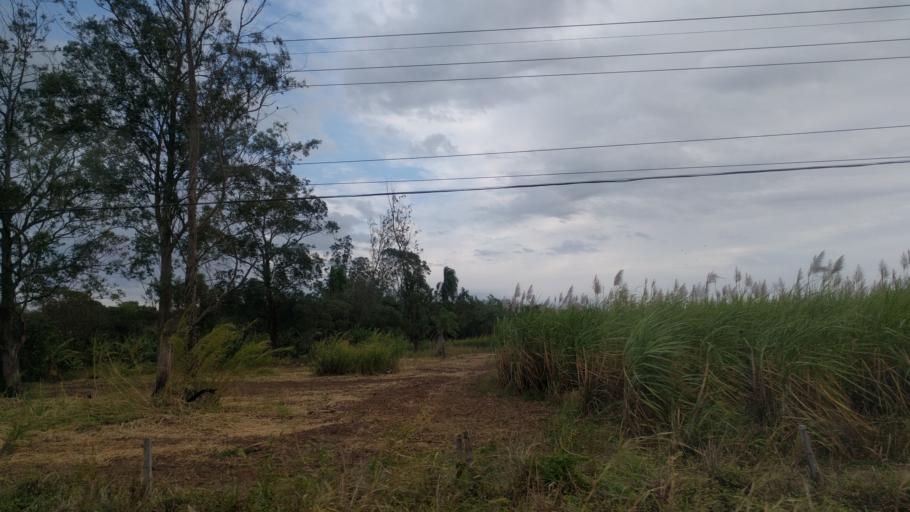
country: BO
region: Santa Cruz
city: Montero
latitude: -17.3916
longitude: -63.2163
